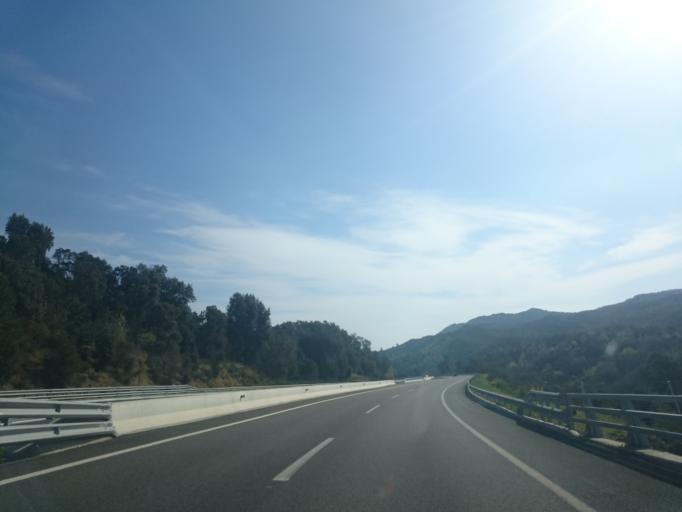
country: ES
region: Catalonia
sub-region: Provincia de Girona
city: Sant Hilari Sacalm
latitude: 41.8502
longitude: 2.5556
